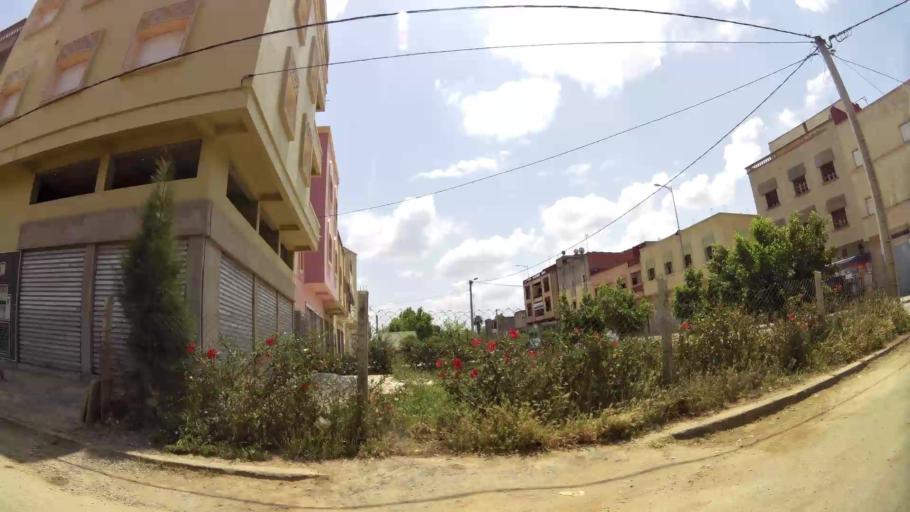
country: MA
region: Rabat-Sale-Zemmour-Zaer
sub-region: Khemisset
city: Tiflet
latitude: 34.0047
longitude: -6.5280
